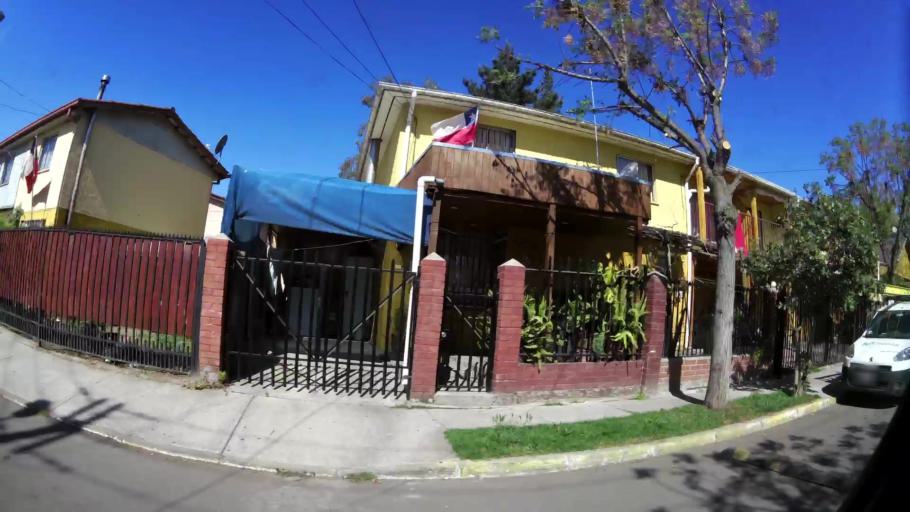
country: CL
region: Santiago Metropolitan
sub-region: Provincia de Talagante
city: Penaflor
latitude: -33.5998
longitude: -70.8919
